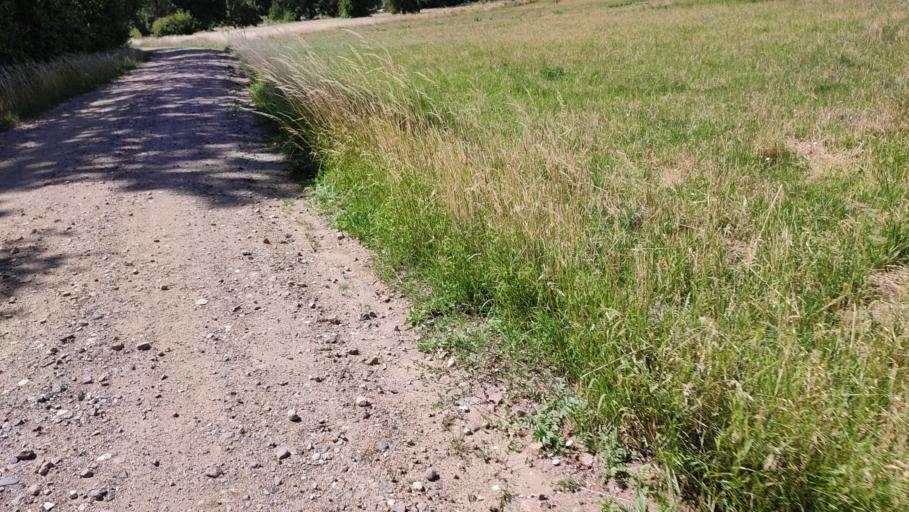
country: DE
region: Lower Saxony
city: Hitzacker
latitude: 53.1994
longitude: 10.9828
